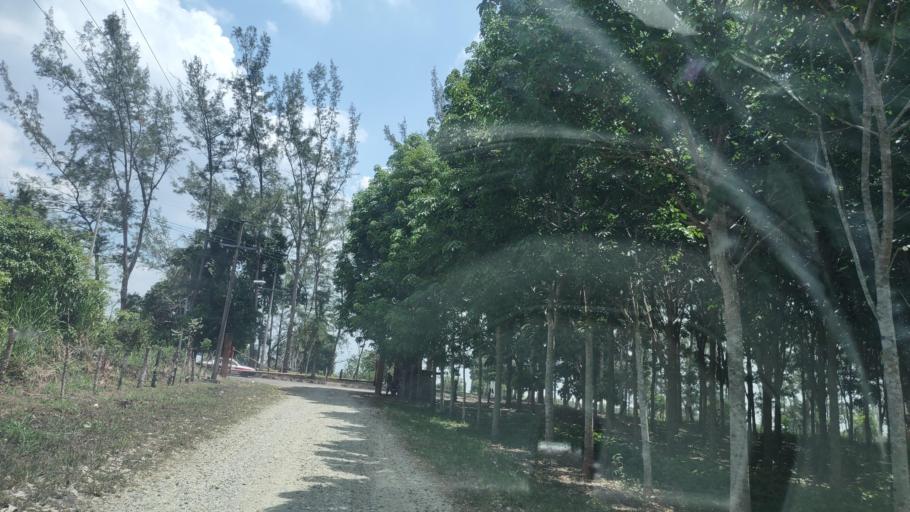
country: MX
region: Veracruz
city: Las Choapas
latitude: 17.9313
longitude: -94.1539
